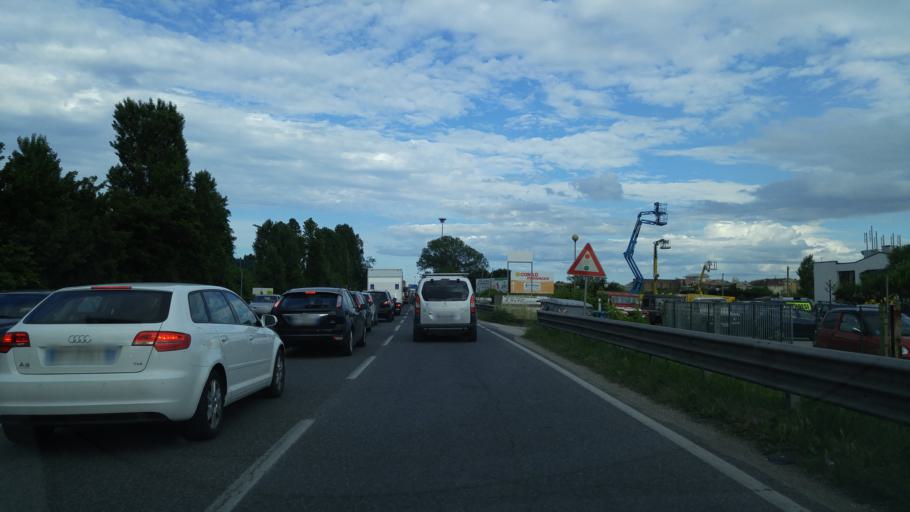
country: IT
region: Emilia-Romagna
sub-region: Provincia di Rimini
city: Rimini
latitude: 44.0422
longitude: 12.5677
